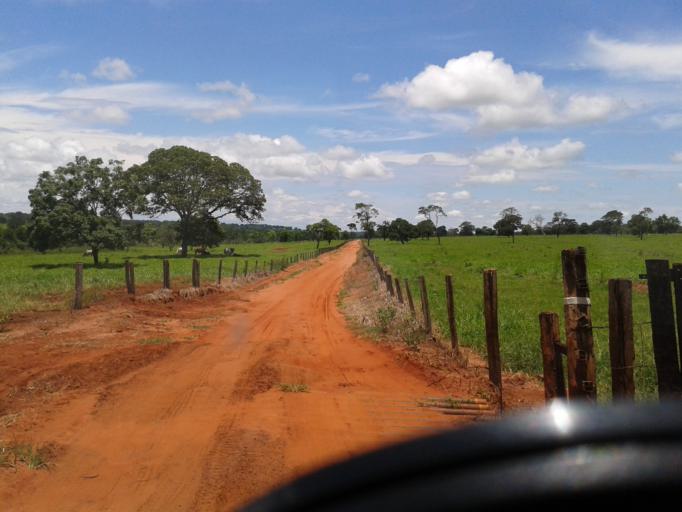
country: BR
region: Minas Gerais
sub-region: Santa Vitoria
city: Santa Vitoria
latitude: -18.9450
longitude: -49.8617
